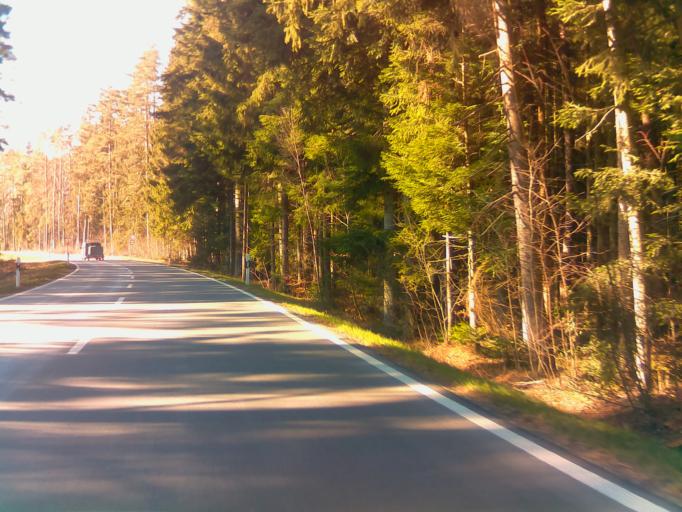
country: DE
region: Baden-Wuerttemberg
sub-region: Karlsruhe Region
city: Neuweiler
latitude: 48.6690
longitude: 8.6076
